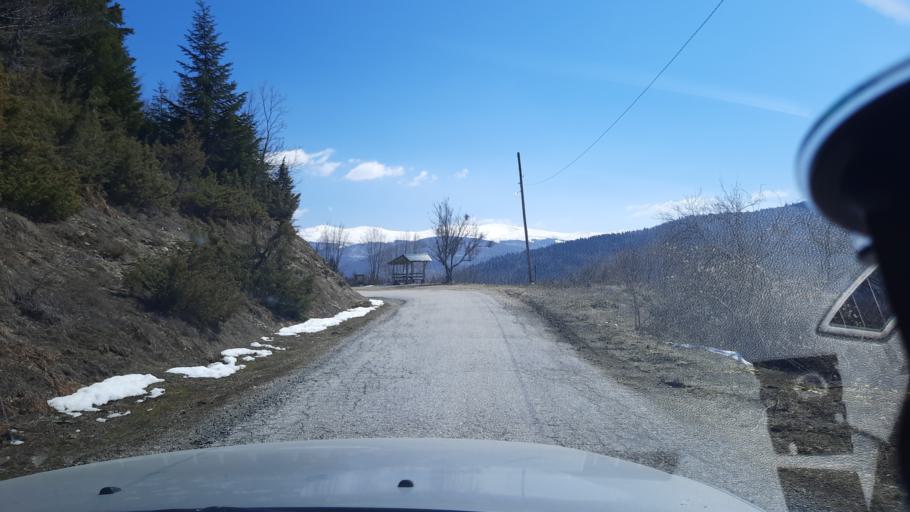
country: MK
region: Gostivar
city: Vrutok
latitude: 41.7106
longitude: 20.7319
